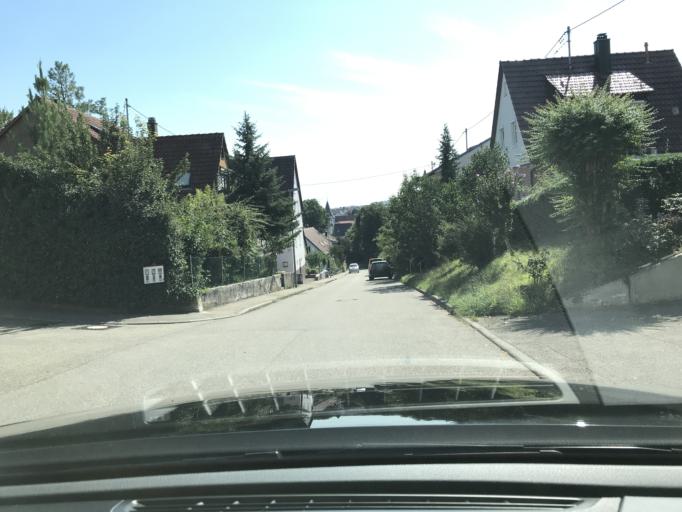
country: DE
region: Baden-Wuerttemberg
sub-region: Regierungsbezirk Stuttgart
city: Affalterbach
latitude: 48.8937
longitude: 9.3143
